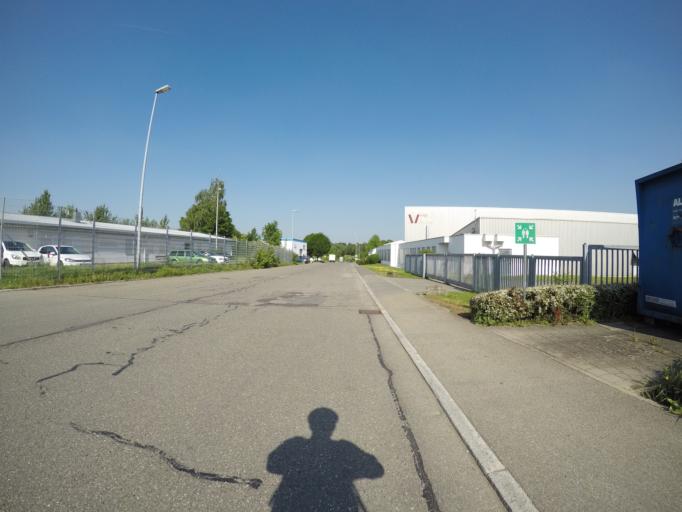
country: DE
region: Baden-Wuerttemberg
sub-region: Tuebingen Region
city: Wannweil
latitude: 48.4999
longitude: 9.1538
